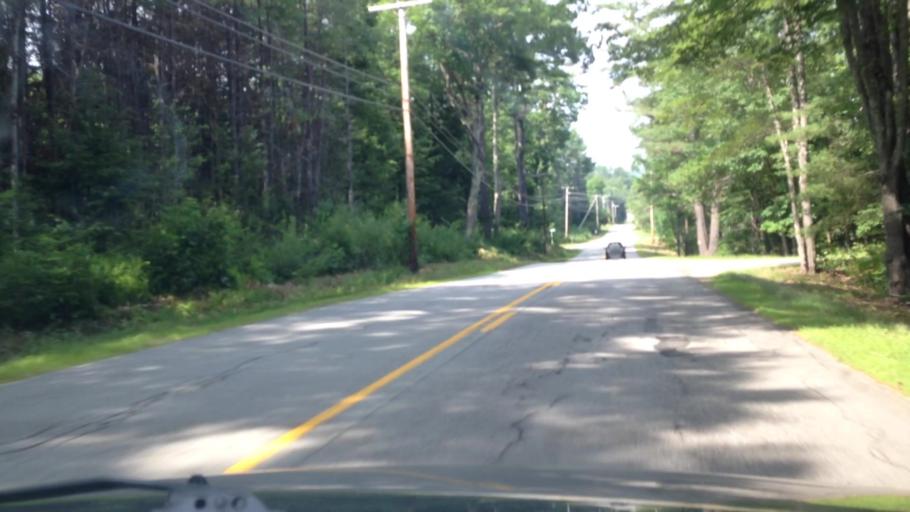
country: US
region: New Hampshire
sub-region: Cheshire County
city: Swanzey
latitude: 42.8618
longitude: -72.2456
